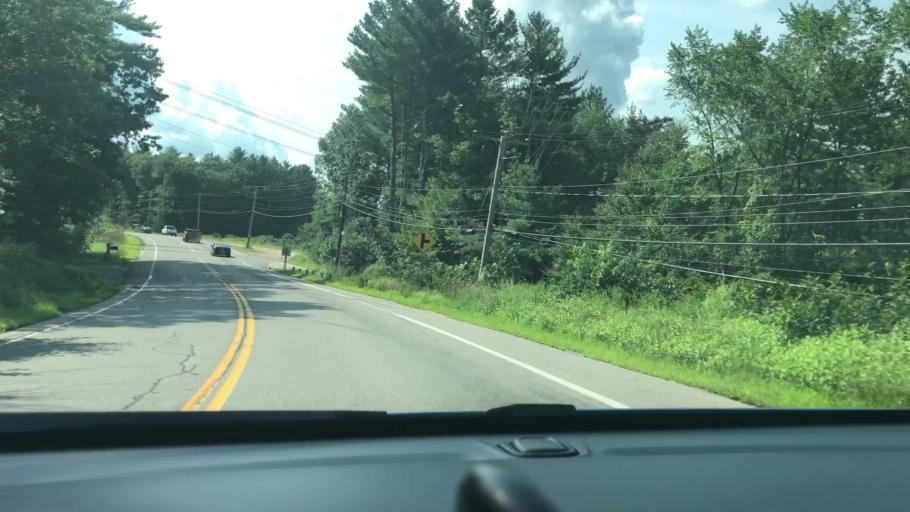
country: US
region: New Hampshire
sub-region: Hillsborough County
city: Goffstown
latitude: 43.0146
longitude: -71.5554
